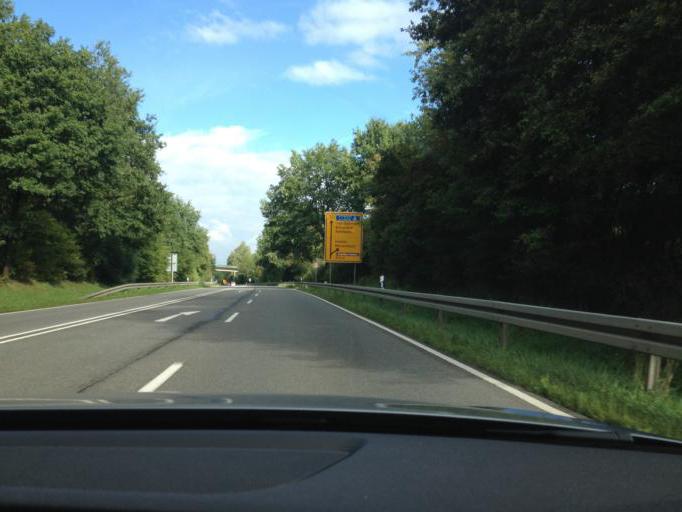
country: DE
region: Saarland
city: Namborn
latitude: 49.4973
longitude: 7.1511
